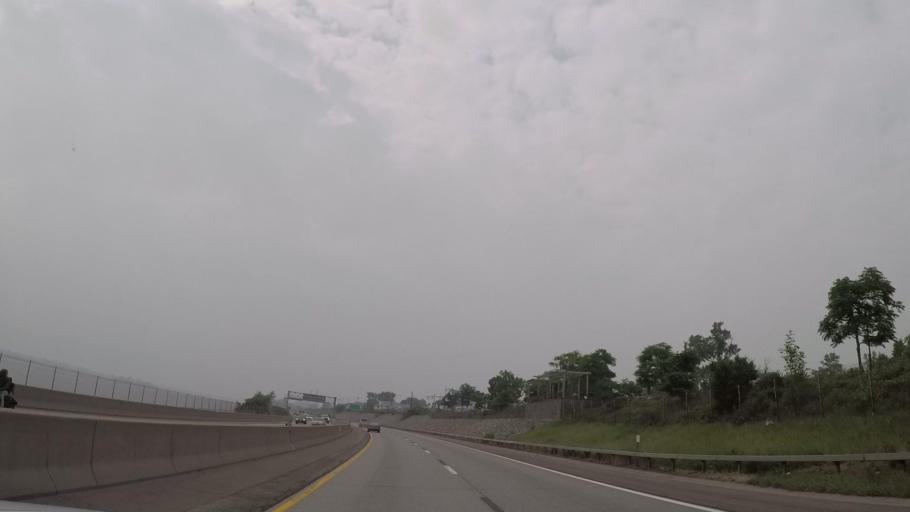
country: US
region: New York
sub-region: Erie County
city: Kenmore
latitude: 42.9552
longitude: -78.9111
